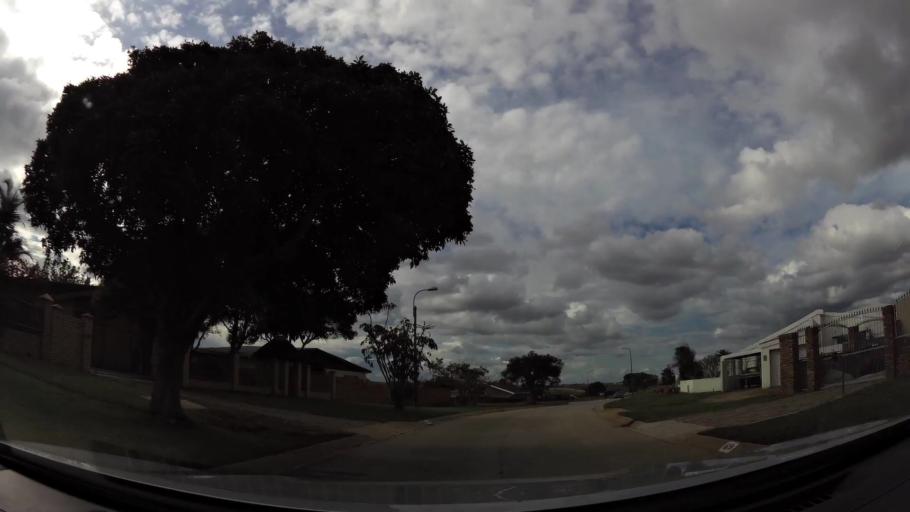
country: ZA
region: Eastern Cape
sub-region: Nelson Mandela Bay Metropolitan Municipality
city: Port Elizabeth
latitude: -33.9331
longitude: 25.5081
